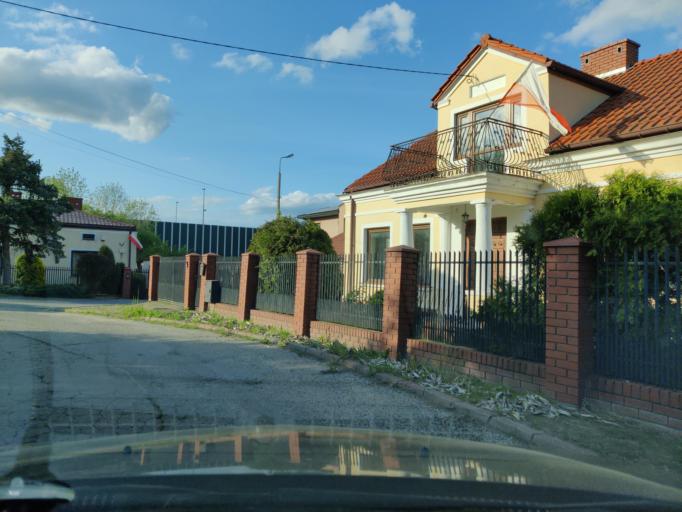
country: PL
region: Masovian Voivodeship
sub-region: Warszawa
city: Kabaty
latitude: 52.1296
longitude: 21.0837
